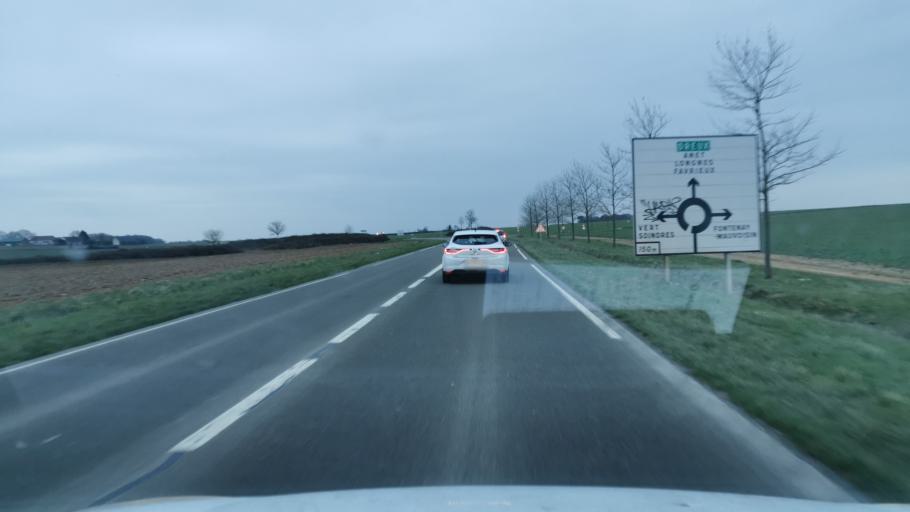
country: FR
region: Ile-de-France
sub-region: Departement des Yvelines
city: Magnanville
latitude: 48.9575
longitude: 1.6643
